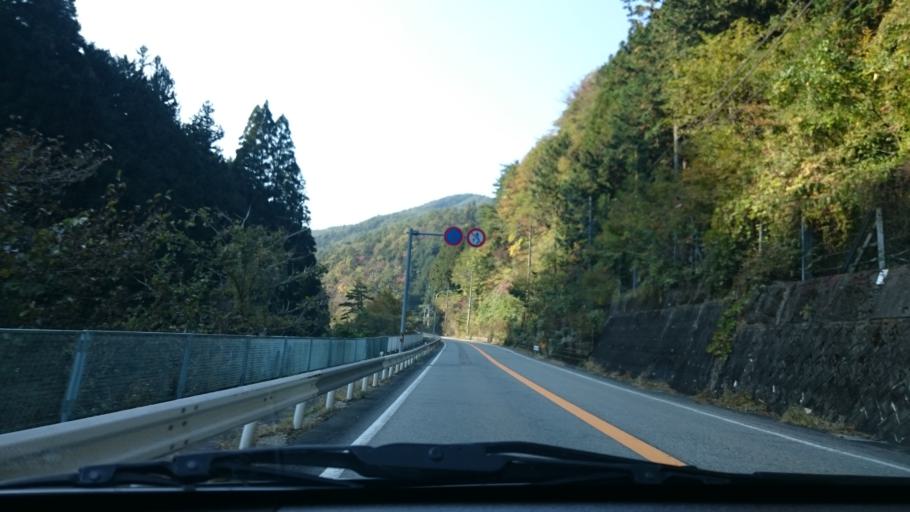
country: JP
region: Gifu
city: Gujo
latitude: 35.7698
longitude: 137.2794
